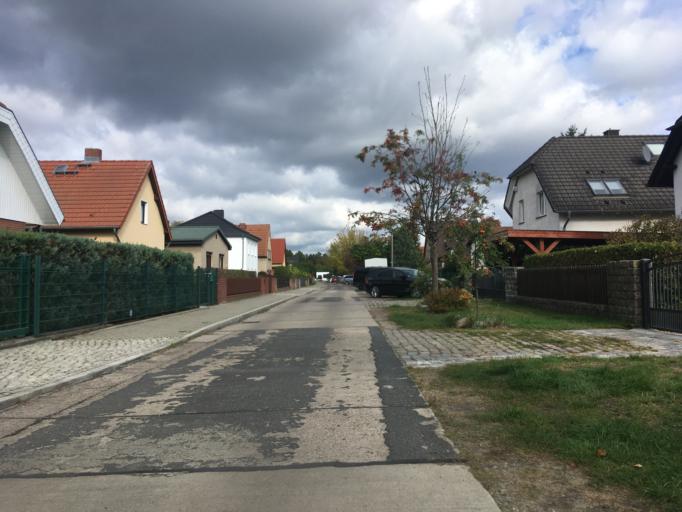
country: DE
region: Berlin
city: Baumschulenweg
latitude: 52.4491
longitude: 13.4817
